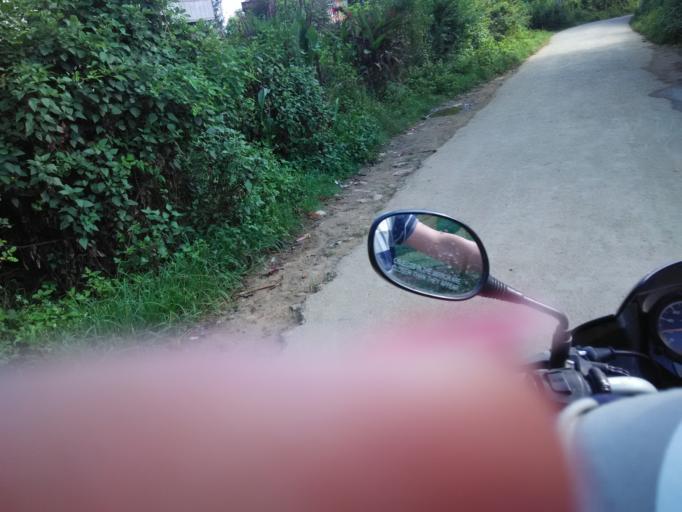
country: NP
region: Central Region
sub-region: Bagmati Zone
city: Patan
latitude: 27.6092
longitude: 85.3316
